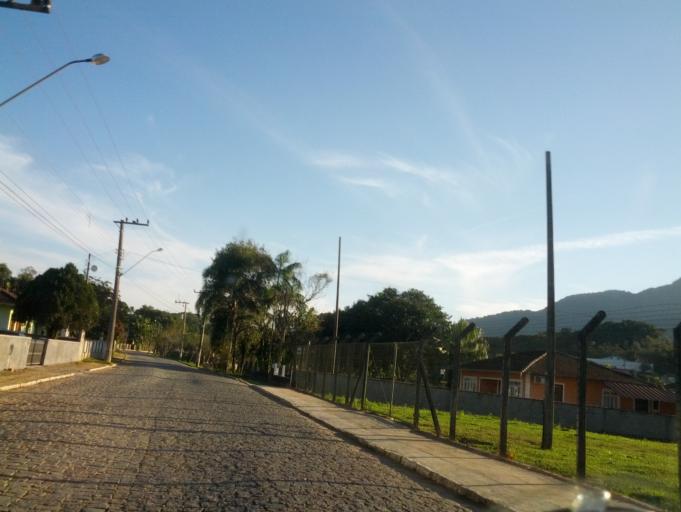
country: BR
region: Santa Catarina
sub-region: Indaial
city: Indaial
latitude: -26.9044
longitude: -49.2597
